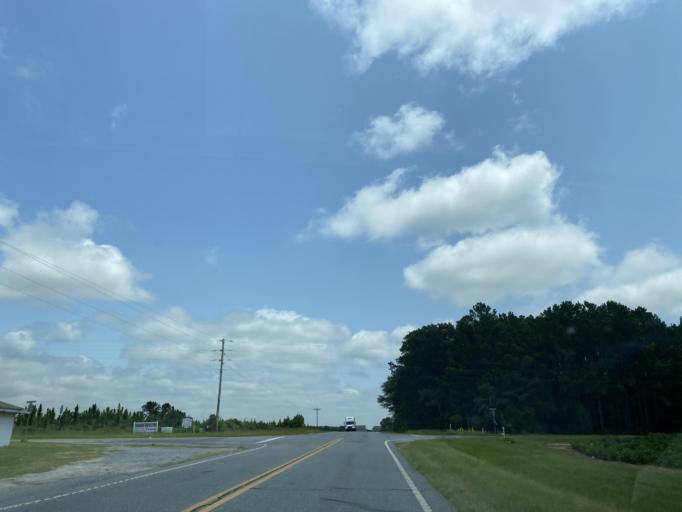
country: US
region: Georgia
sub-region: Telfair County
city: McRae
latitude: 32.0962
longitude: -82.8524
